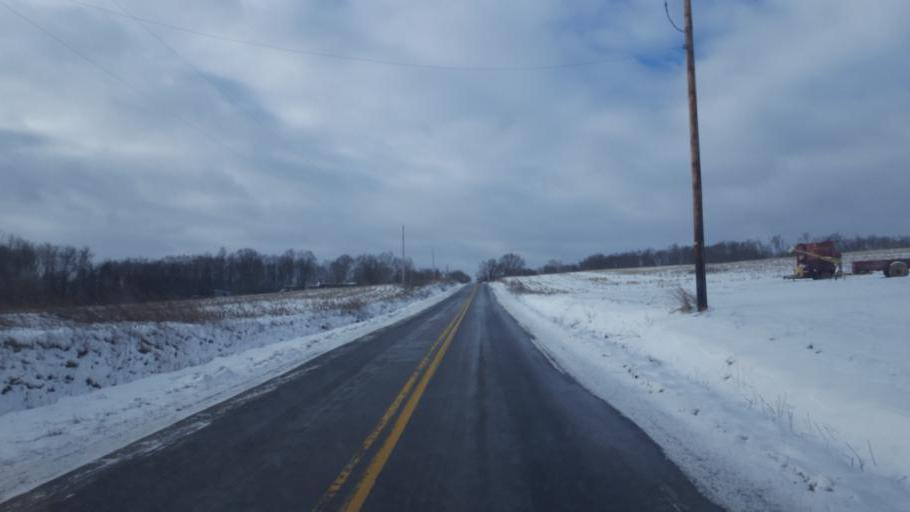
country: US
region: Pennsylvania
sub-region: Mercer County
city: Mercer
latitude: 41.1769
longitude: -80.2464
